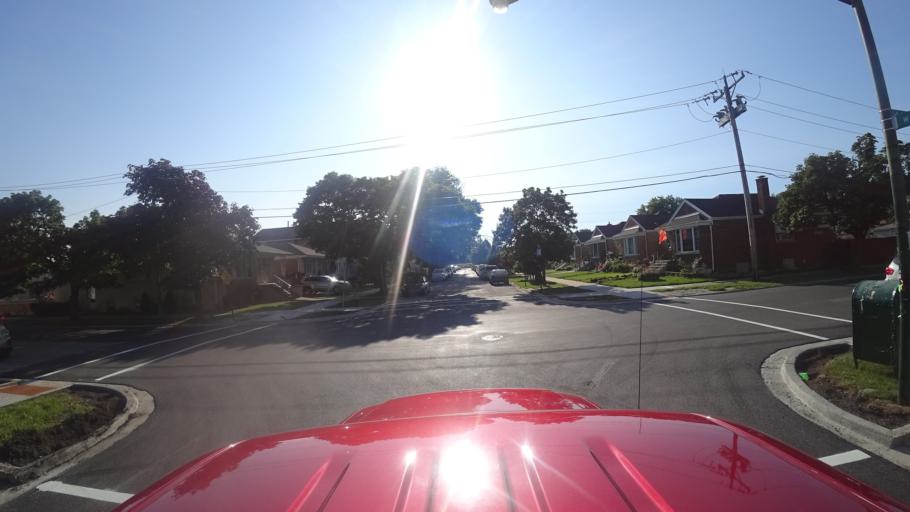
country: US
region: Illinois
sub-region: Cook County
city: Hometown
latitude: 41.7913
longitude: -87.7161
